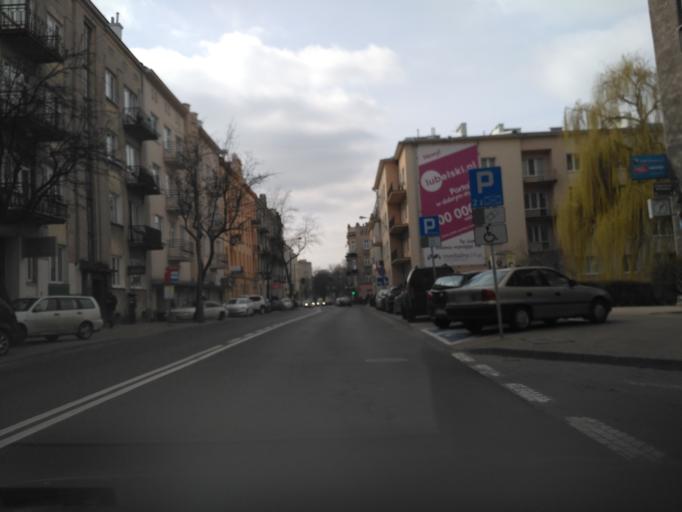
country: PL
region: Lublin Voivodeship
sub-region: Powiat lubelski
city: Lublin
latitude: 51.2453
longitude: 22.5556
